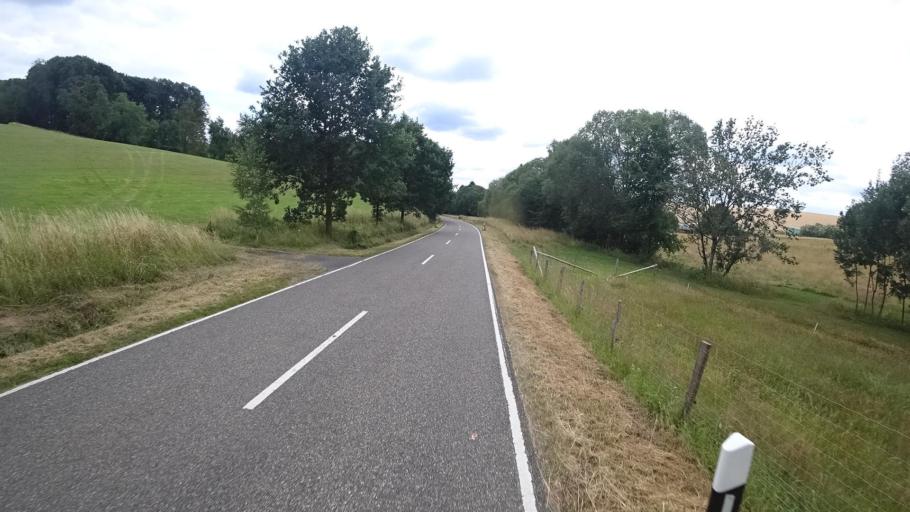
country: DE
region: Rheinland-Pfalz
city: Birnbach
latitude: 50.7016
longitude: 7.5837
